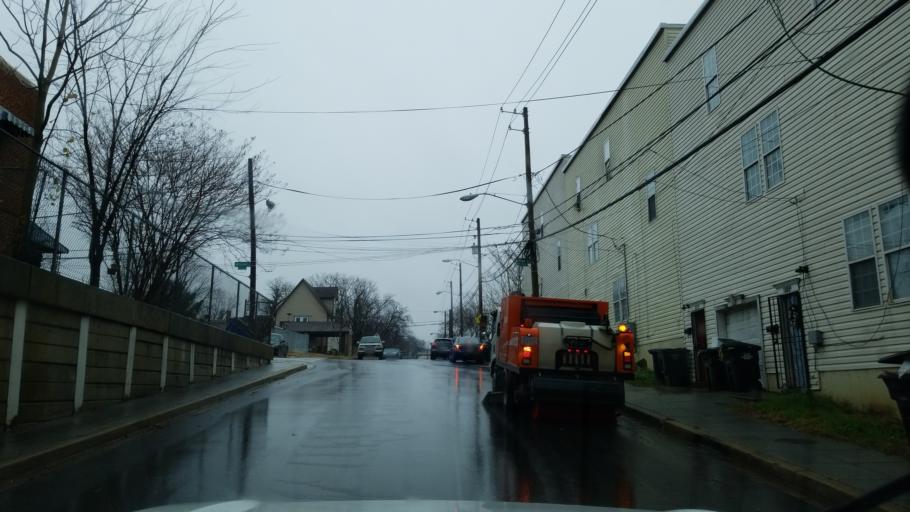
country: US
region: Maryland
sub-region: Prince George's County
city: Hillcrest Heights
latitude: 38.8600
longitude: -76.9898
